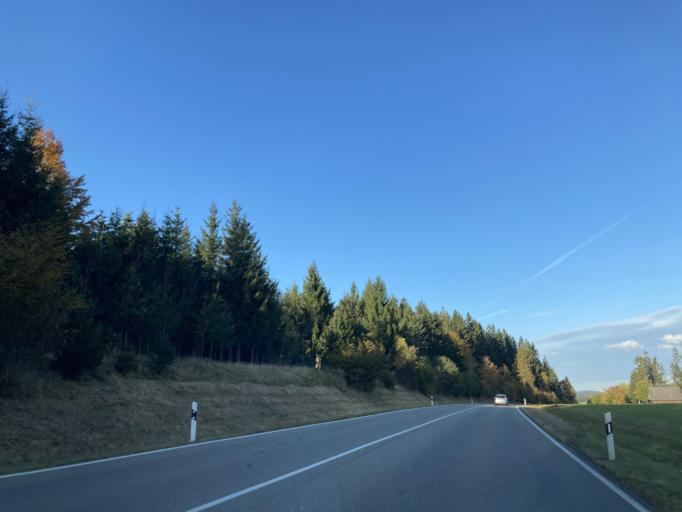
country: DE
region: Baden-Wuerttemberg
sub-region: Freiburg Region
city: Sankt Margen
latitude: 47.9765
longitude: 8.1311
